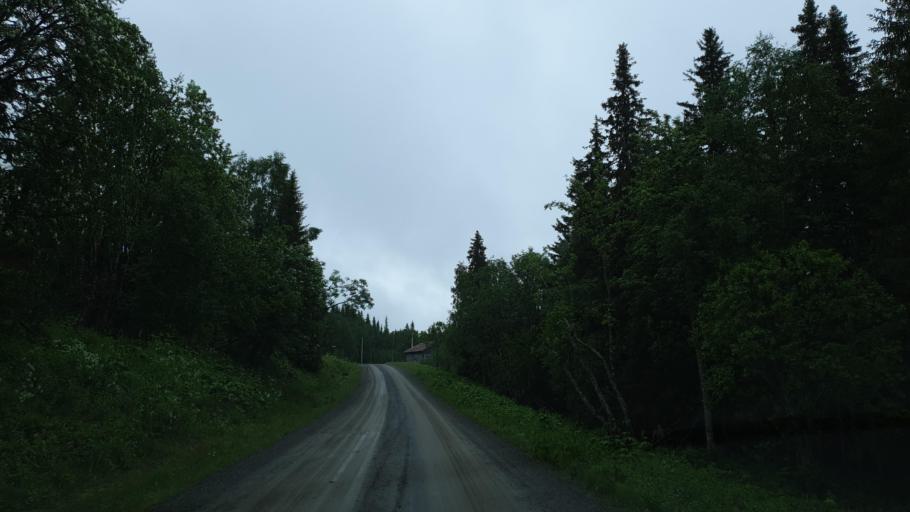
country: SE
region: Vaesterbotten
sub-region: Vilhelmina Kommun
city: Sjoberg
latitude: 65.3359
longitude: 15.8958
